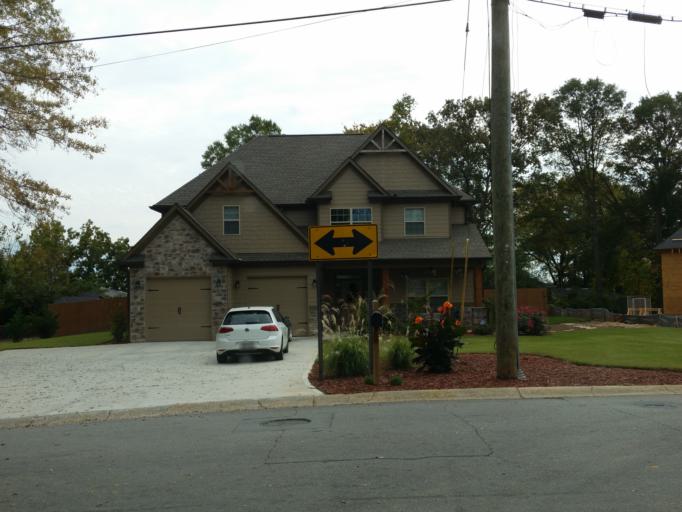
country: US
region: Georgia
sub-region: Cobb County
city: Marietta
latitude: 33.9453
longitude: -84.5376
